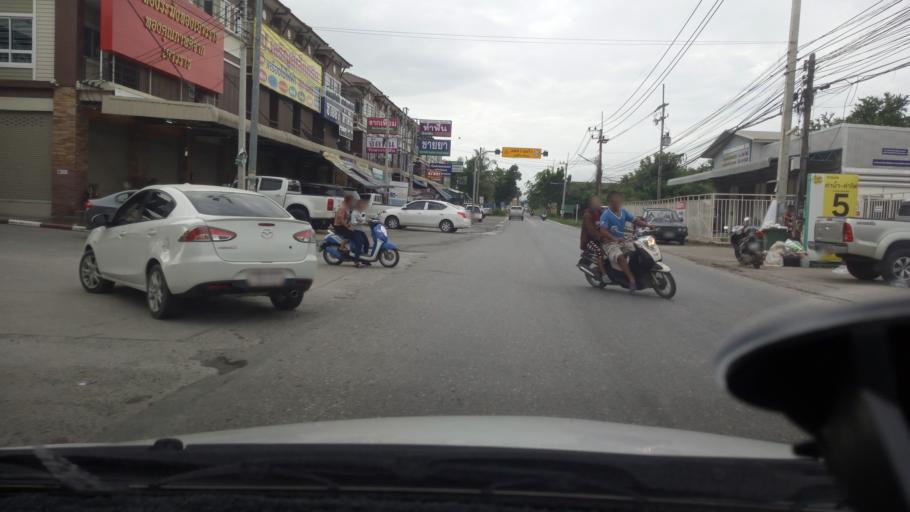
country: TH
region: Chon Buri
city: Chon Buri
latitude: 13.4013
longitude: 101.0485
